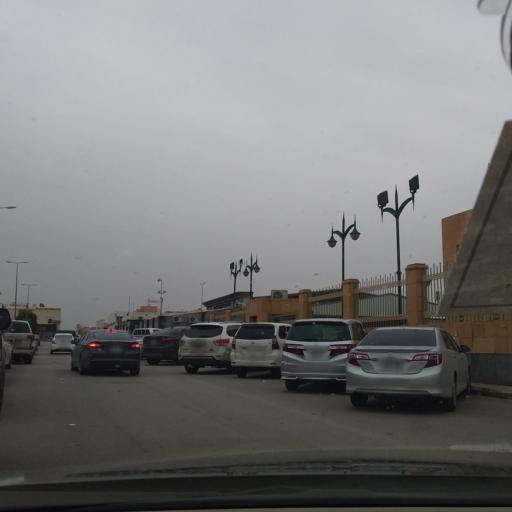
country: SA
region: Ar Riyad
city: Riyadh
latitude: 24.7304
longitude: 46.7732
